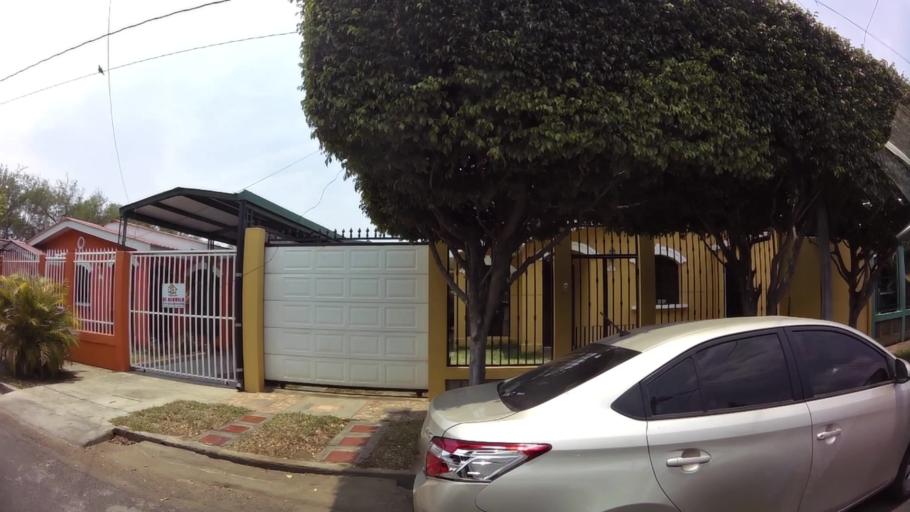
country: NI
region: Managua
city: Managua
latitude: 12.1185
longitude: -86.2861
